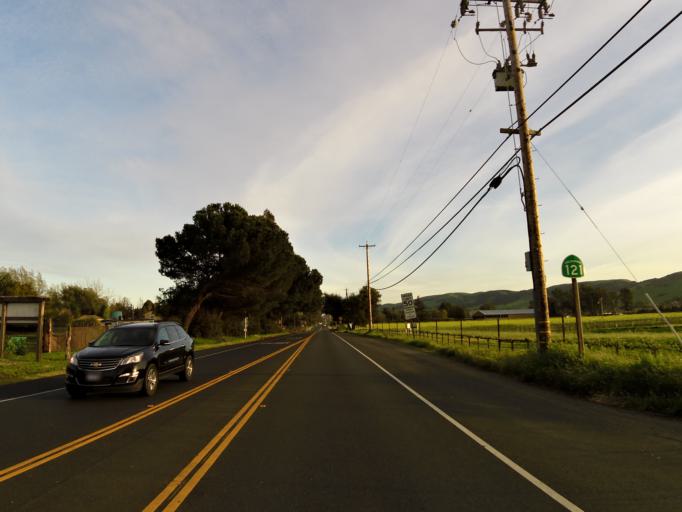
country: US
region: California
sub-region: Sonoma County
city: Temelec
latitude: 38.2350
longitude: -122.4611
